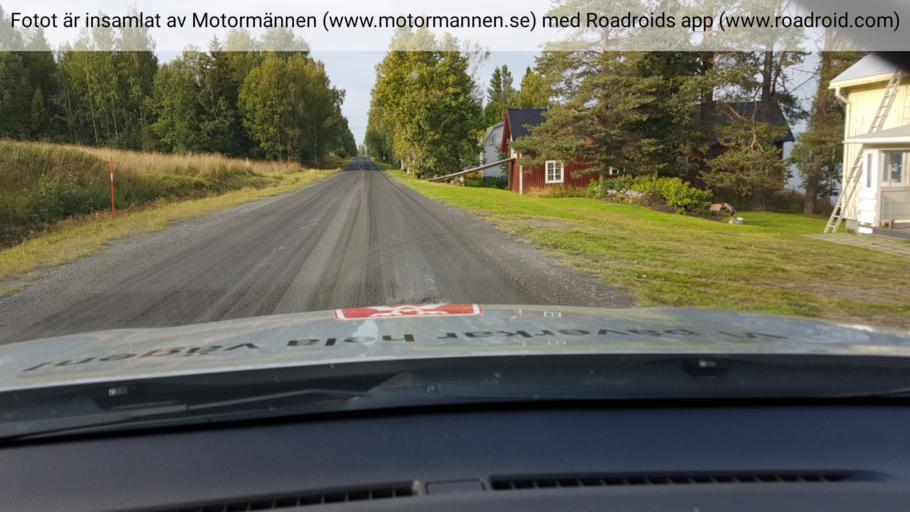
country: SE
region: Jaemtland
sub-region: Stroemsunds Kommun
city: Stroemsund
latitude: 64.1137
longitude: 15.8131
